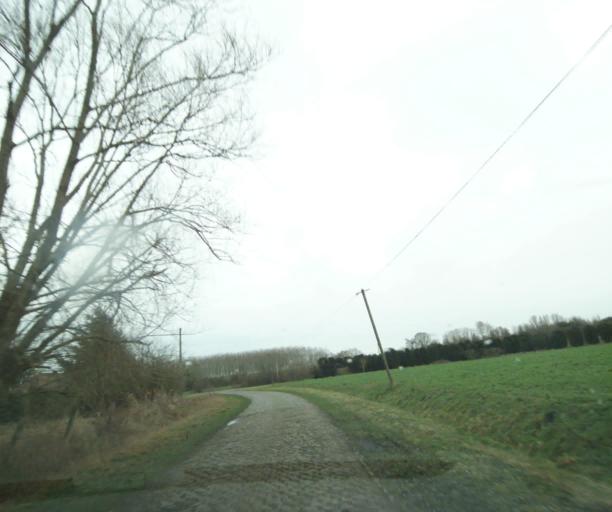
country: FR
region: Nord-Pas-de-Calais
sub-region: Departement du Nord
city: Vicq
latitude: 50.4222
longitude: 3.6158
